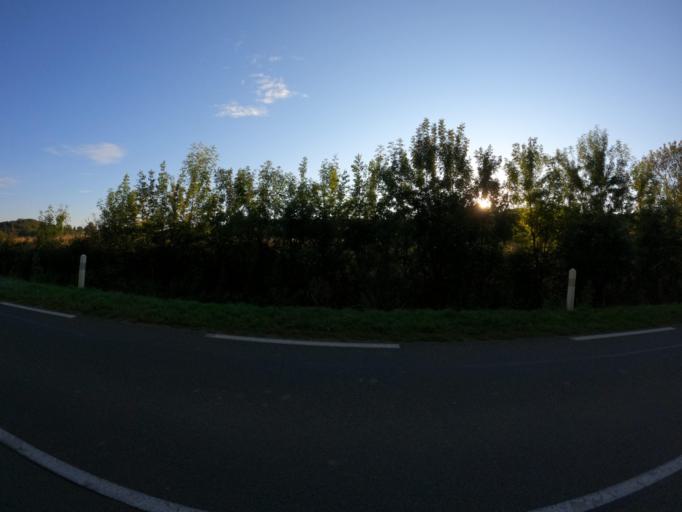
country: FR
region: Pays de la Loire
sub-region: Departement de la Vendee
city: Sainte-Hermine
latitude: 46.5786
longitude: -1.1075
